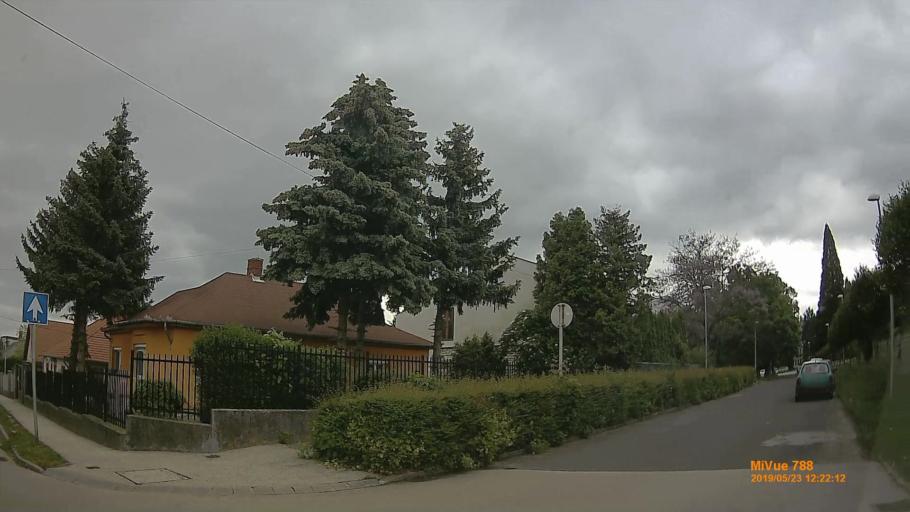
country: HU
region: Veszprem
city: Veszprem
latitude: 47.0857
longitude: 17.9053
